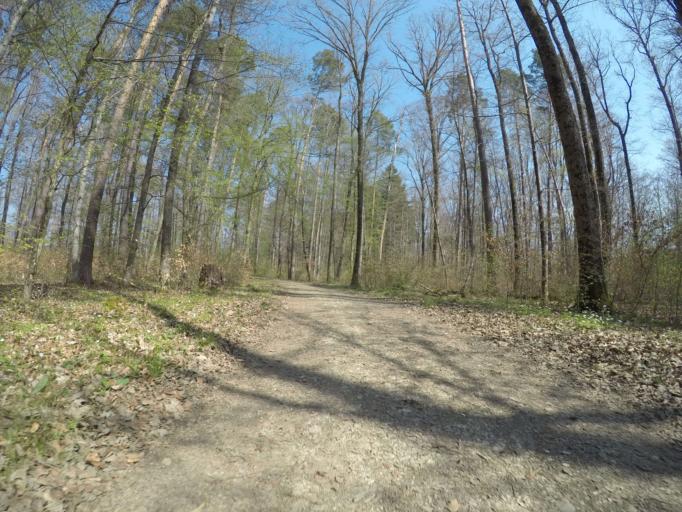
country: DE
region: Baden-Wuerttemberg
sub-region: Tuebingen Region
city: Gomaringen
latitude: 48.4676
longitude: 9.1413
